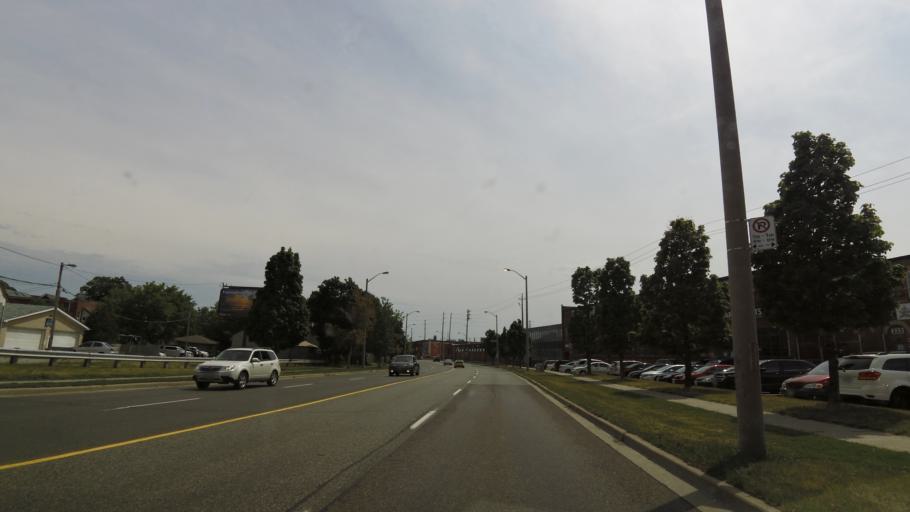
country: CA
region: Ontario
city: Etobicoke
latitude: 43.6051
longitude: -79.5067
